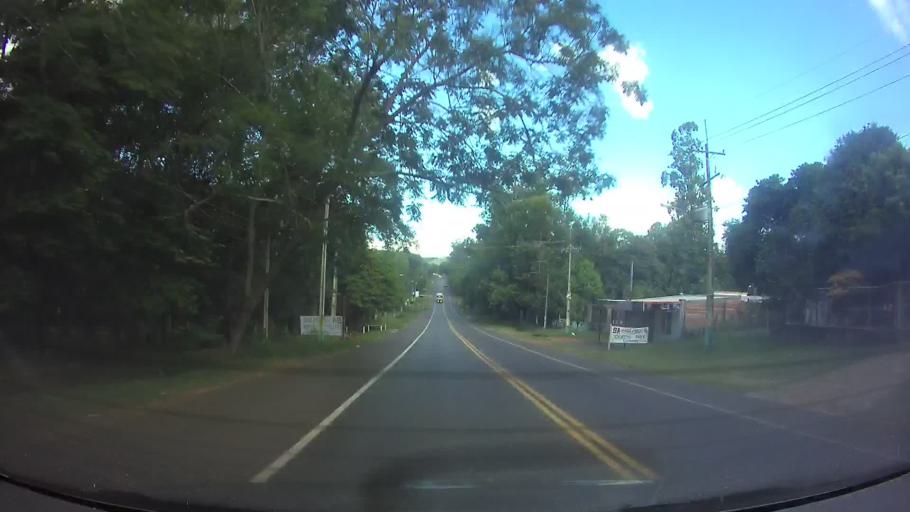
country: PY
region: Cordillera
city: Caacupe
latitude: -25.3850
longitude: -57.1241
